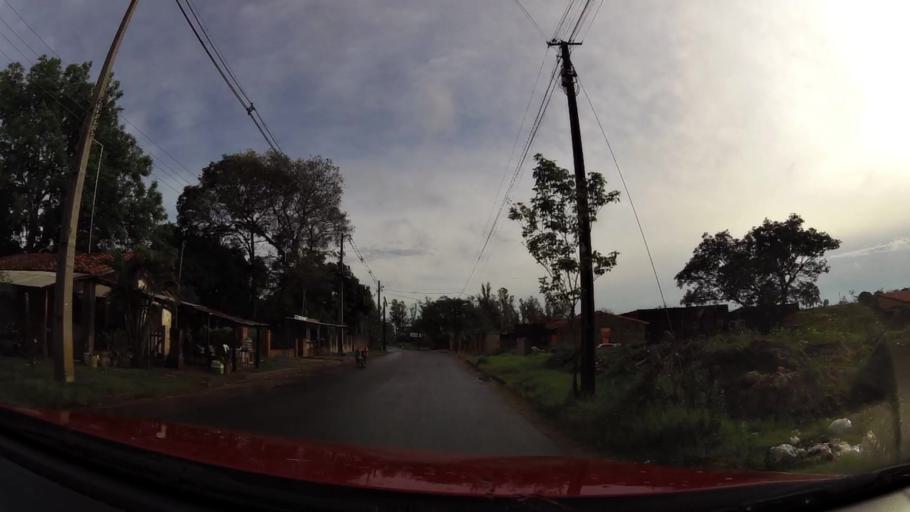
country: PY
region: Central
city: Limpio
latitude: -25.1982
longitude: -57.5032
